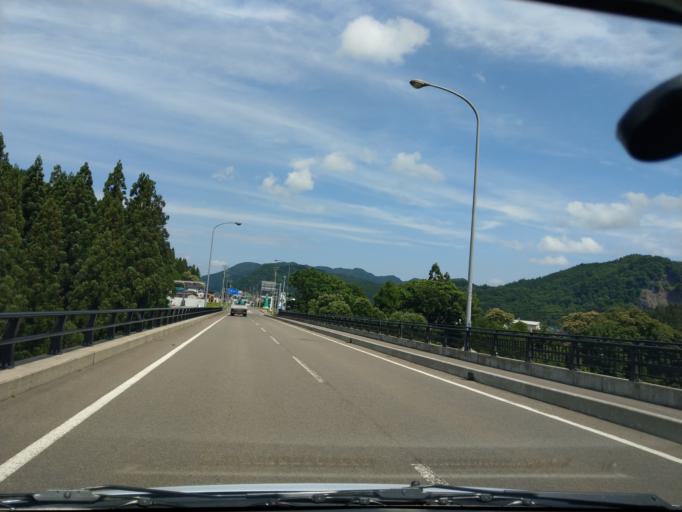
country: JP
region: Akita
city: Kakunodatemachi
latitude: 39.8995
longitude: 140.4584
